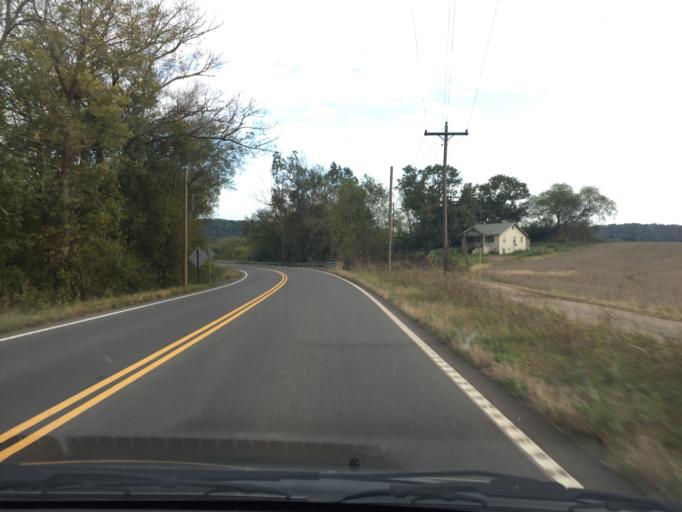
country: US
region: Tennessee
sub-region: Monroe County
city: Sweetwater
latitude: 35.6259
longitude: -84.4997
